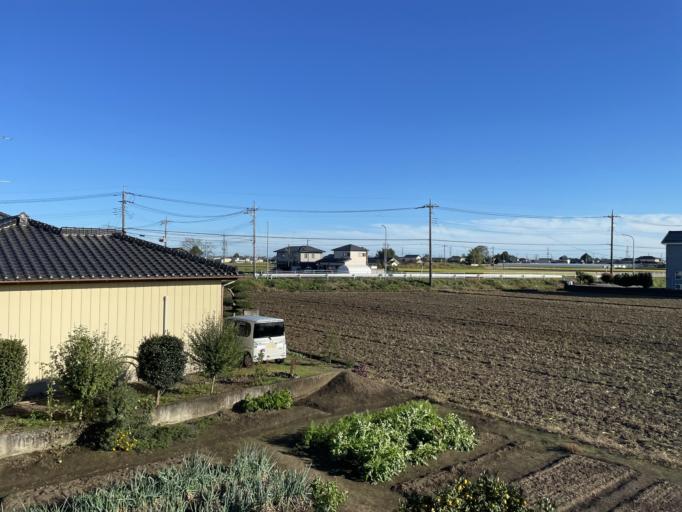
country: JP
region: Tochigi
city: Tochigi
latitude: 36.3602
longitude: 139.7220
